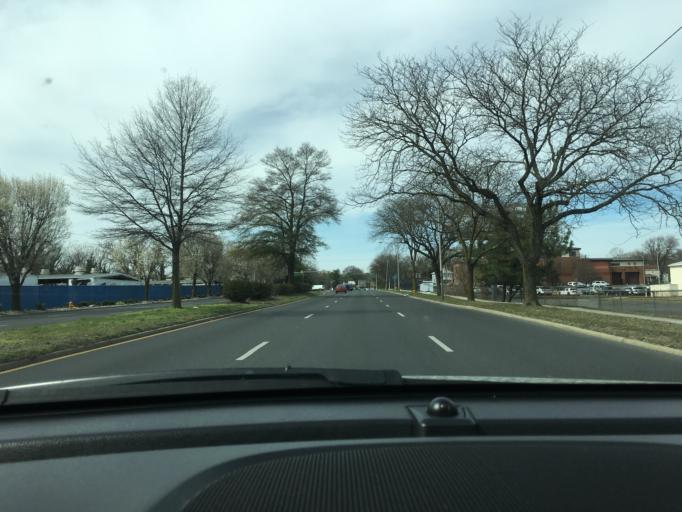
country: US
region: Maryland
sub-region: Wicomico County
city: Salisbury
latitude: 38.3673
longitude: -75.6079
